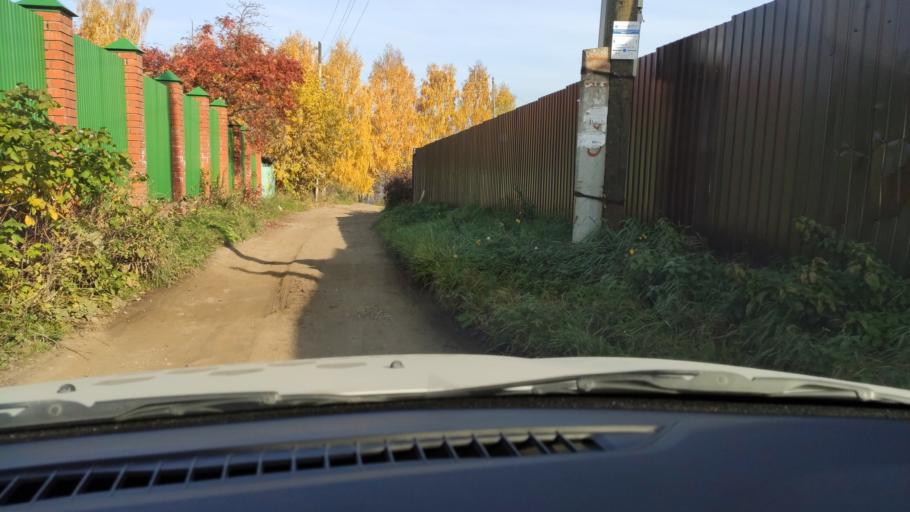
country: RU
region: Perm
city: Sylva
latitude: 58.0479
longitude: 56.7344
